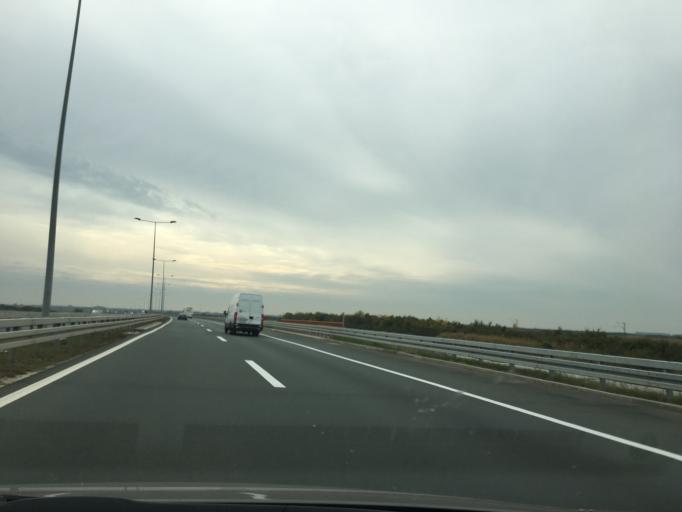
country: RS
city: Dobanovci
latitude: 44.8663
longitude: 20.2537
